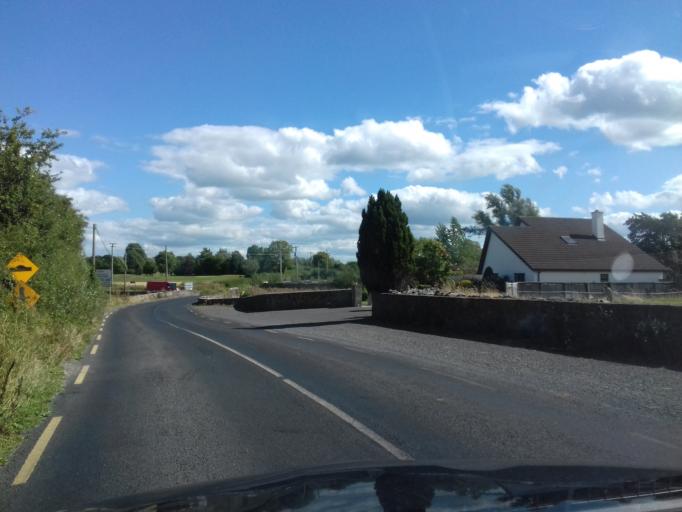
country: IE
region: Leinster
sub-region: Kilkenny
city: Callan
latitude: 52.5357
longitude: -7.3791
